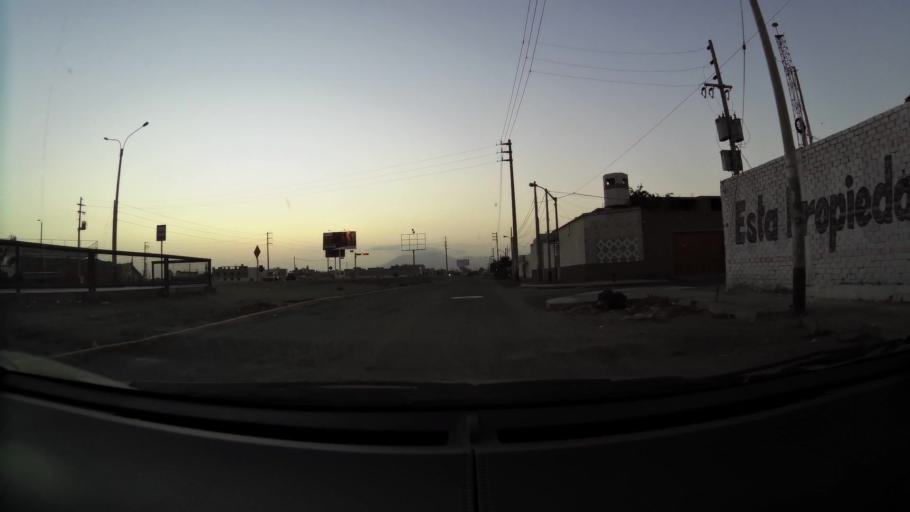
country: PE
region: Ancash
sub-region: Provincia de Santa
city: Buenos Aires
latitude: -9.1253
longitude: -78.5346
